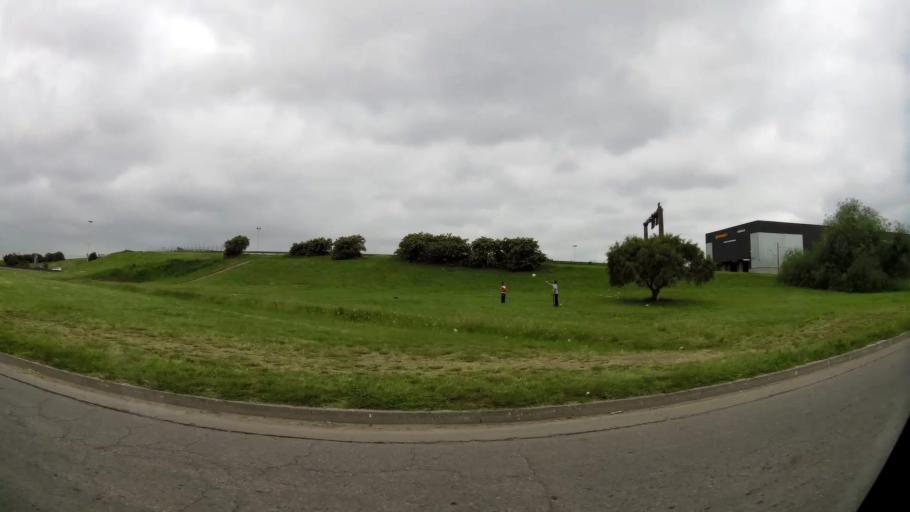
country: AR
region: Buenos Aires
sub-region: Partido de Ezeiza
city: Ezeiza
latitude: -34.8350
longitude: -58.5080
